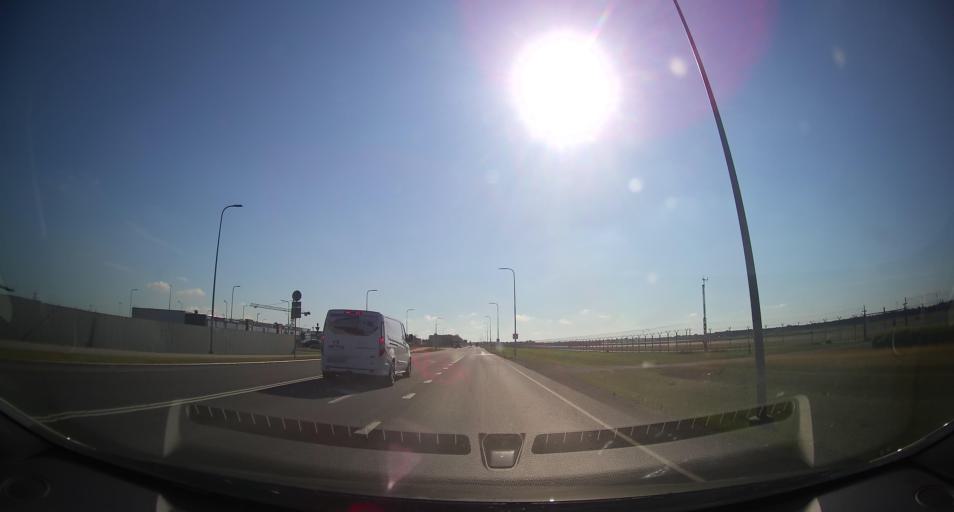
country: EE
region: Harju
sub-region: Tallinna linn
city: Kose
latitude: 59.4162
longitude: 24.8489
